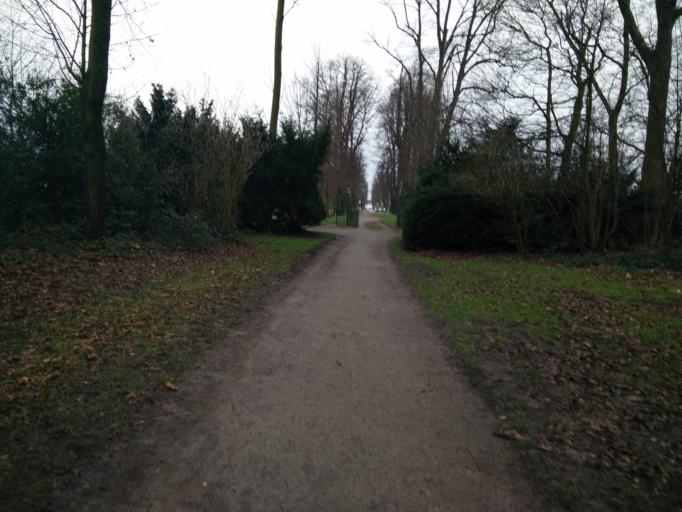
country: DE
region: North Rhine-Westphalia
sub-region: Regierungsbezirk Dusseldorf
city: Dusseldorf
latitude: 51.3045
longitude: 6.7542
